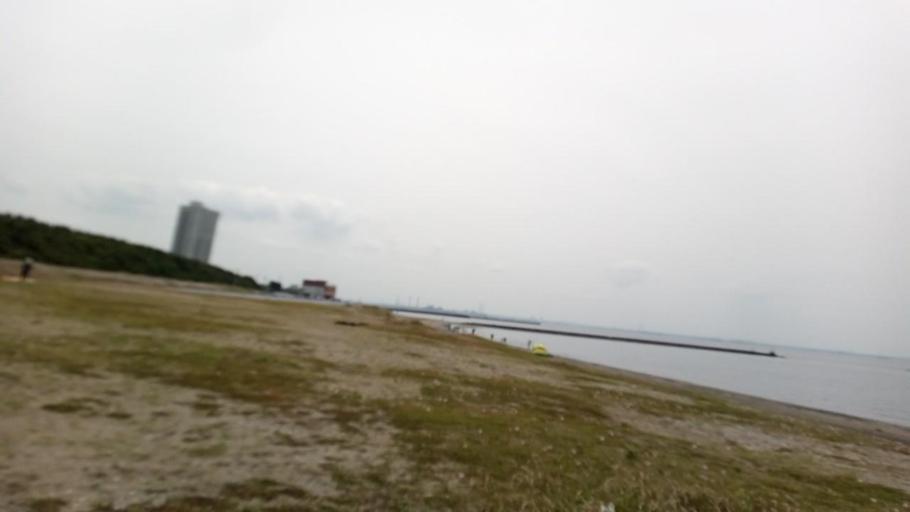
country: JP
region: Chiba
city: Funabashi
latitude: 35.6394
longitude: 140.0354
